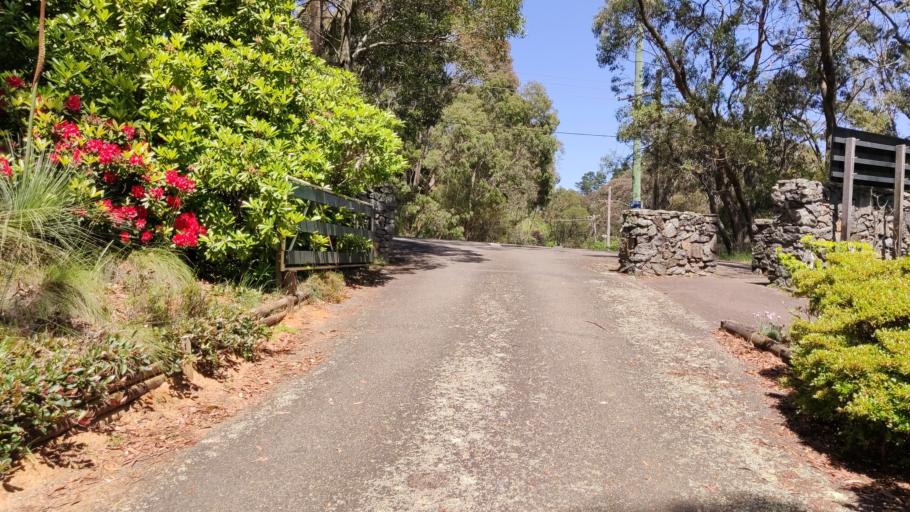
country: AU
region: New South Wales
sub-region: Blue Mountains Municipality
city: Blackheath
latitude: -33.6275
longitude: 150.2883
